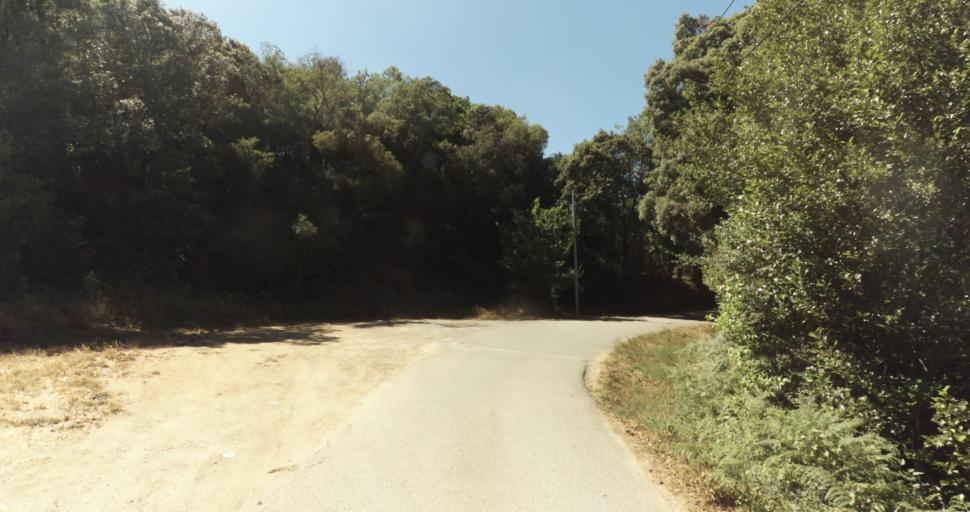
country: FR
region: Provence-Alpes-Cote d'Azur
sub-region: Departement du Var
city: Gassin
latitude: 43.2306
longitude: 6.5676
